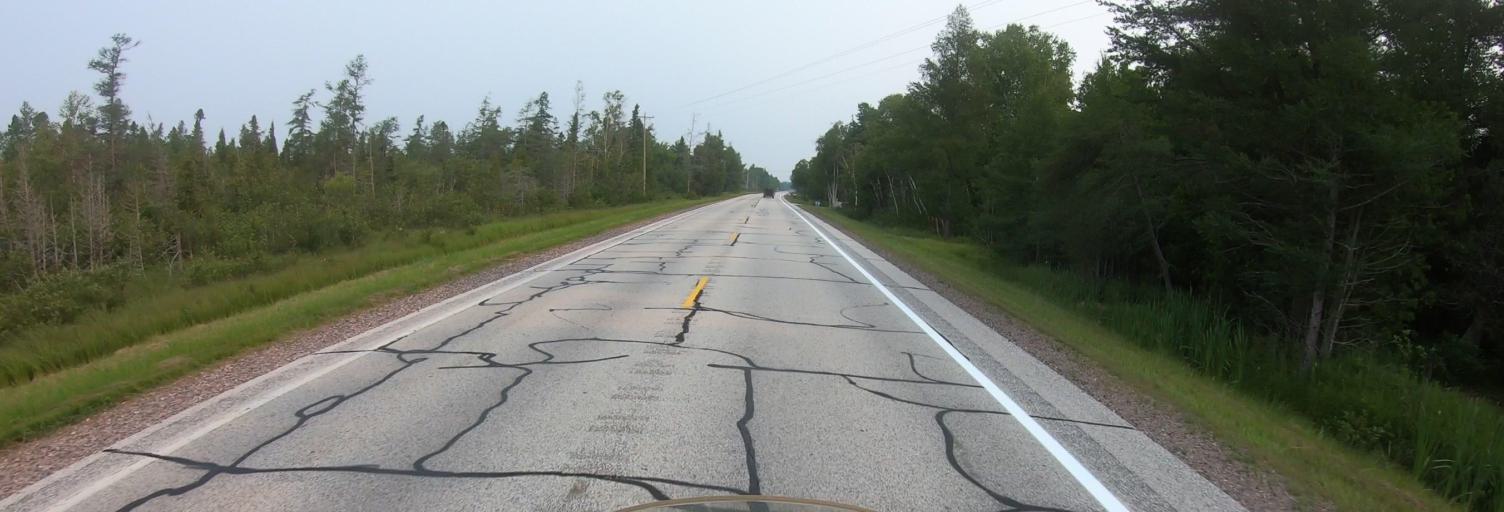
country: US
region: Michigan
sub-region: Luce County
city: Newberry
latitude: 46.5768
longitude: -85.0355
